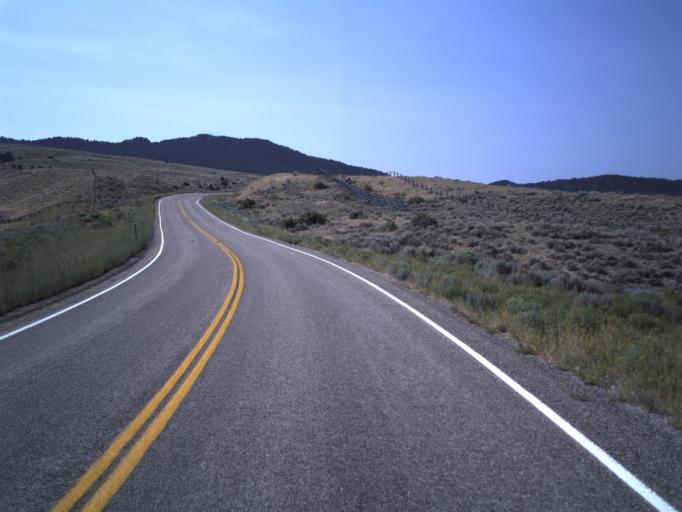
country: US
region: Utah
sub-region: Daggett County
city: Manila
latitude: 40.9738
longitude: -109.4635
